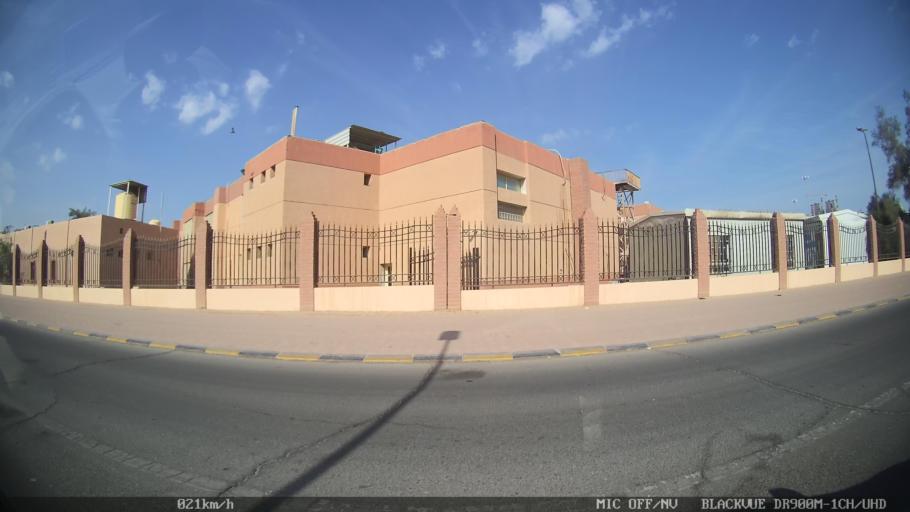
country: KW
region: Muhafazat Hawalli
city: Hawalli
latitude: 29.3432
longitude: 48.0271
